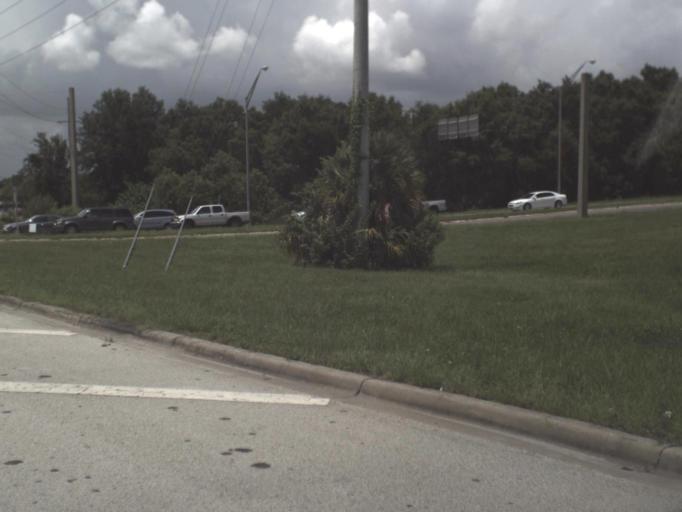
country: US
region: Florida
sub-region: Hillsborough County
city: Carrollwood
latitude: 28.0368
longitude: -82.5062
